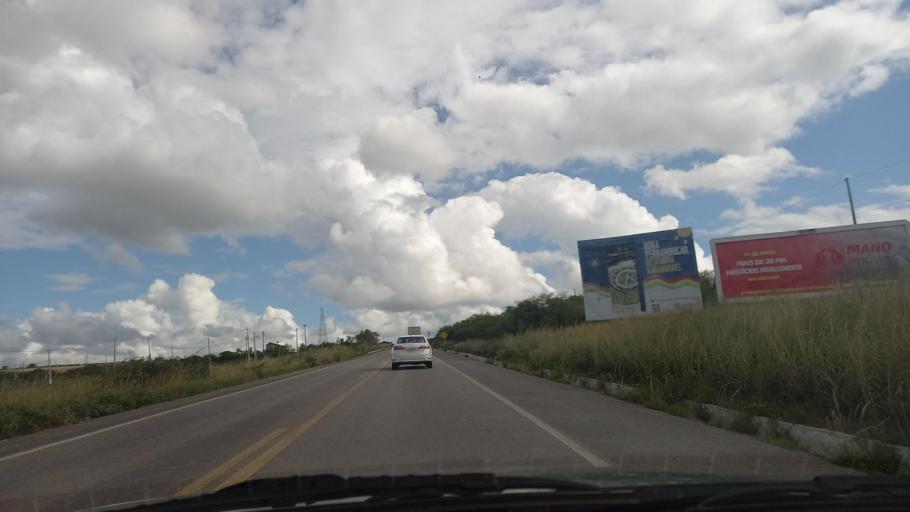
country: BR
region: Pernambuco
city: Garanhuns
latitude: -8.8288
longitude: -36.4520
